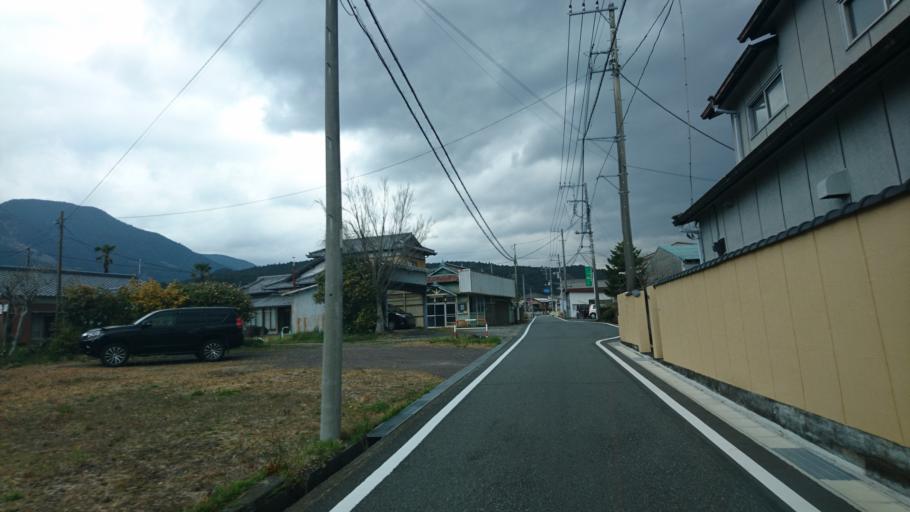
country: JP
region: Shizuoka
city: Fujinomiya
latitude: 35.2847
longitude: 138.5770
